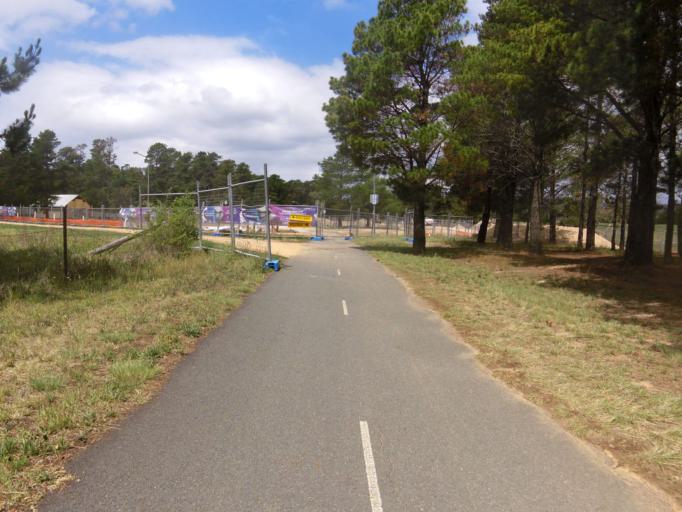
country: AU
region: Australian Capital Territory
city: Macarthur
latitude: -35.4123
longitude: 149.1198
